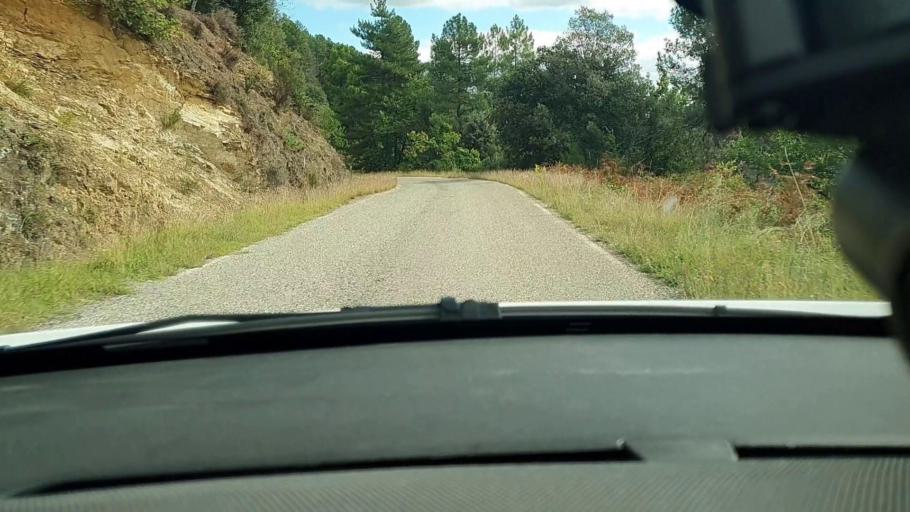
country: FR
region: Languedoc-Roussillon
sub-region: Departement du Gard
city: Besseges
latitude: 44.3103
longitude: 4.0326
